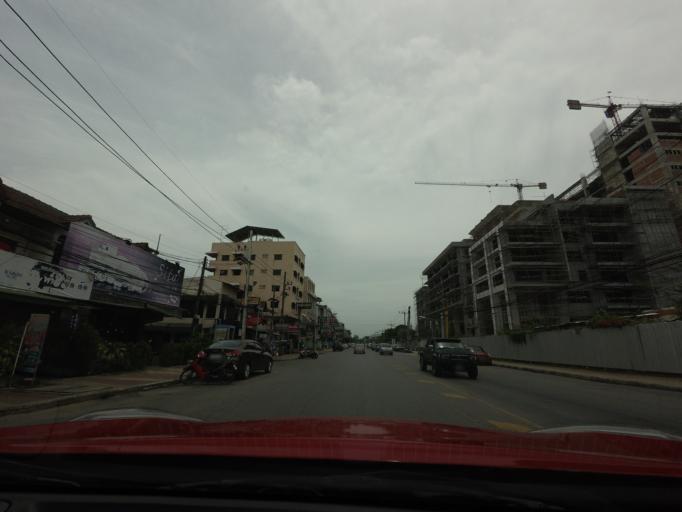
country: TH
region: Songkhla
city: Hat Yai
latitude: 7.0018
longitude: 100.4995
